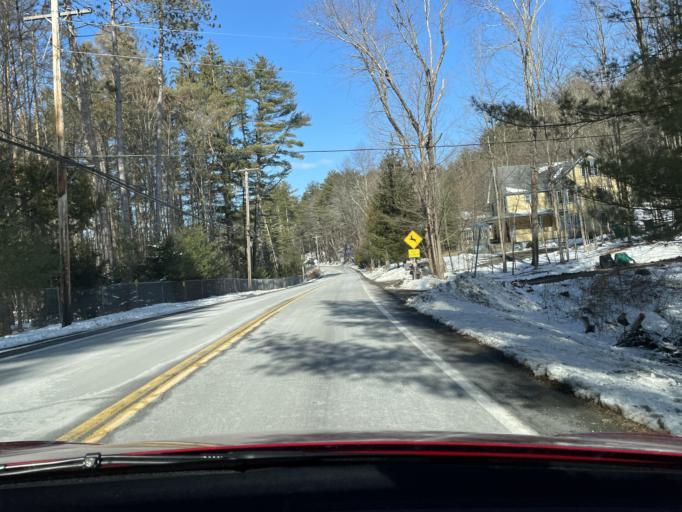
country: US
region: New York
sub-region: Ulster County
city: Woodstock
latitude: 42.0652
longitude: -74.1774
